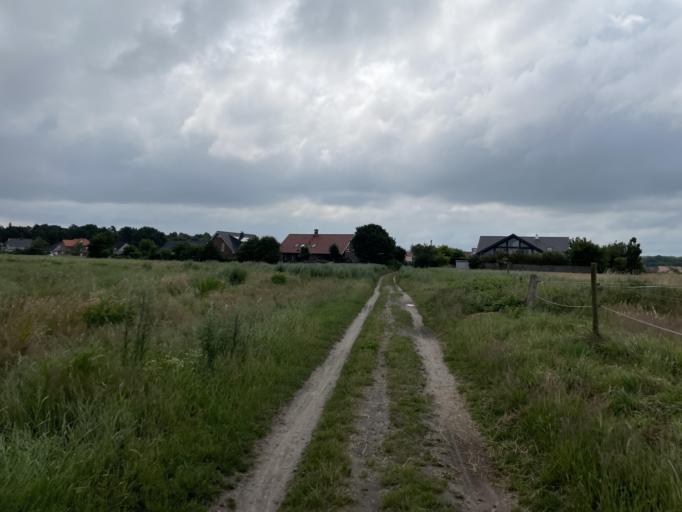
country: DE
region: Lower Saxony
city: Cuxhaven
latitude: 53.8762
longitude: 8.6477
